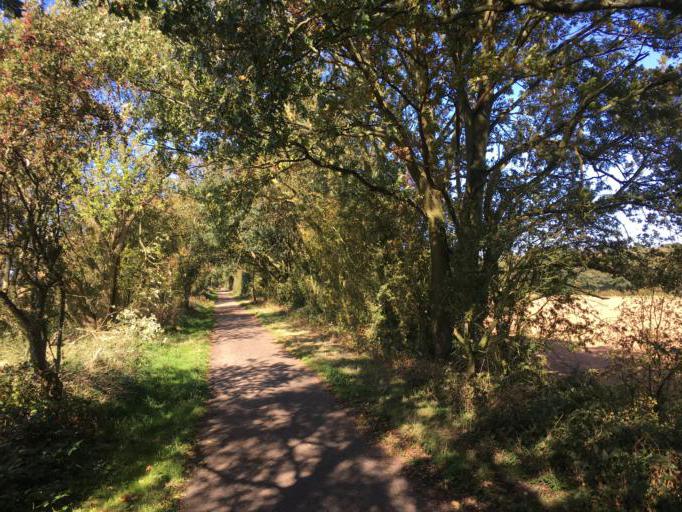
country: GB
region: England
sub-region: Warwickshire
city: Kenilworth
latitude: 52.3694
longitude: -1.5876
